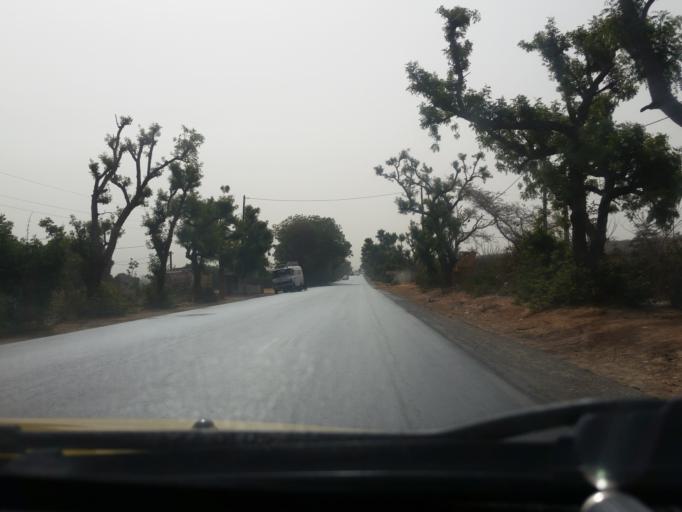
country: SN
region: Thies
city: Pout
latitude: 14.7657
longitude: -17.0920
